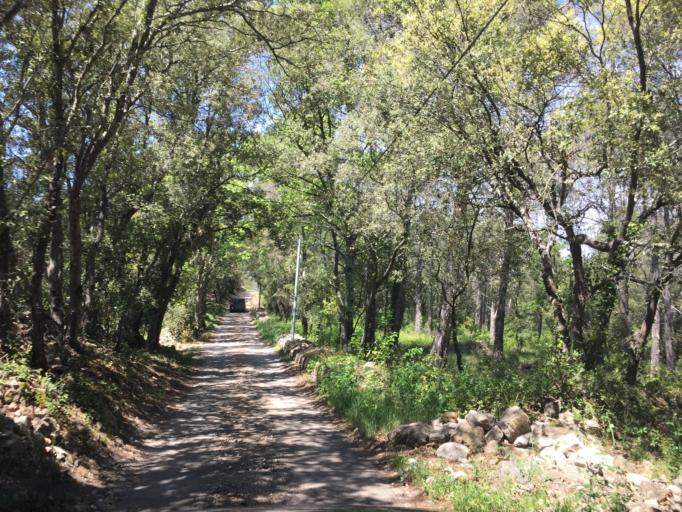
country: FR
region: Provence-Alpes-Cote d'Azur
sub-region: Departement du Var
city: Lorgues
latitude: 43.4721
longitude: 6.3717
